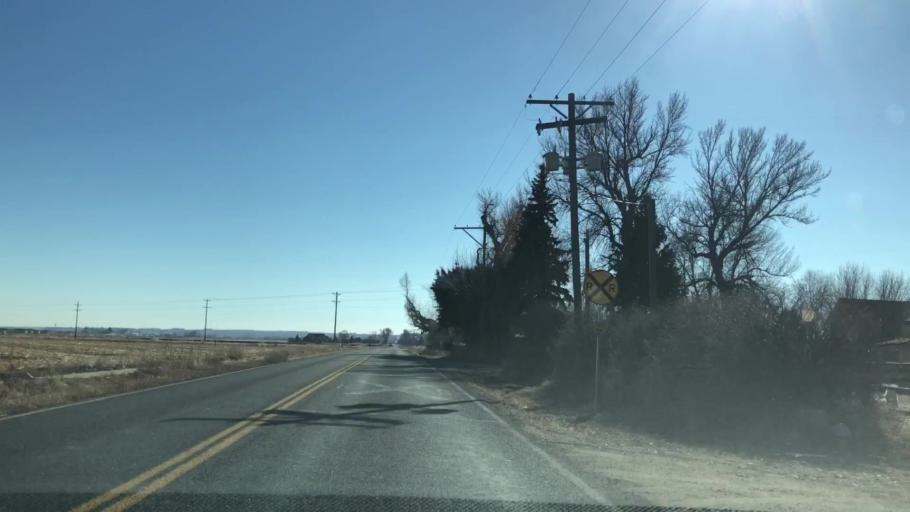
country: US
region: Colorado
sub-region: Weld County
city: Windsor
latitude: 40.5068
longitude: -104.9442
